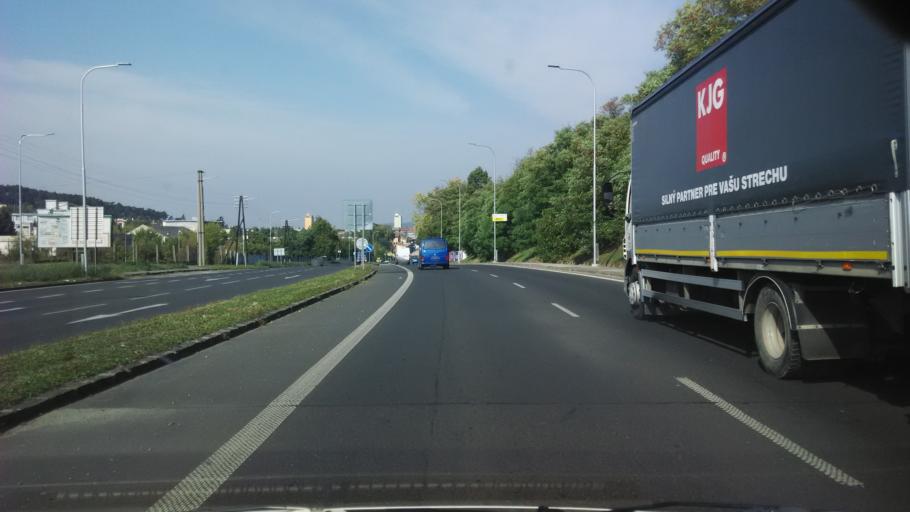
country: SK
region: Nitriansky
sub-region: Okres Nitra
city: Nitra
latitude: 48.2965
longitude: 18.0807
